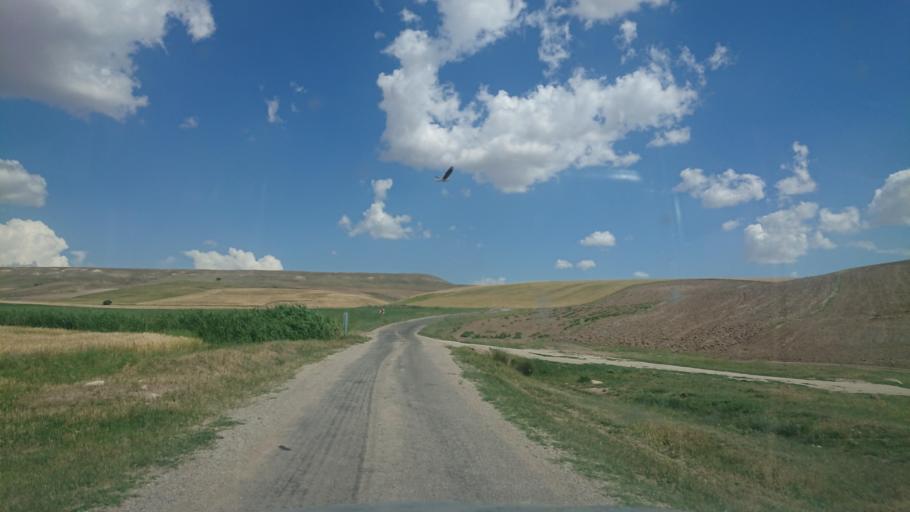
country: TR
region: Aksaray
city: Agacoren
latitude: 38.8148
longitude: 33.7969
